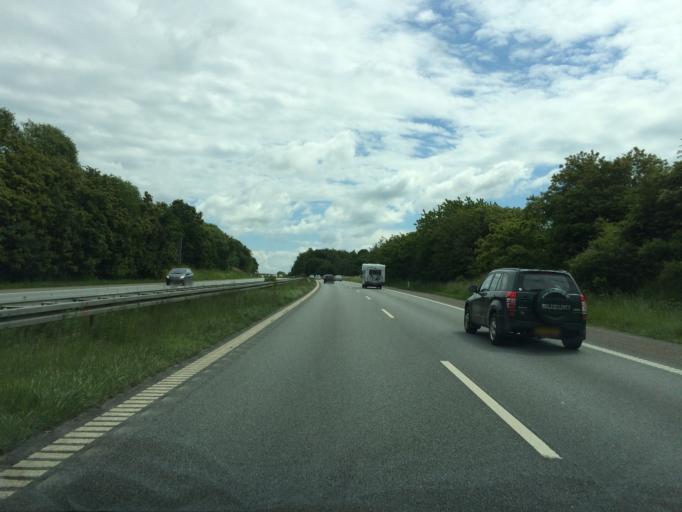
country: DK
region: Zealand
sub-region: Lejre Kommune
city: Lejre
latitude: 55.6437
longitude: 11.9389
